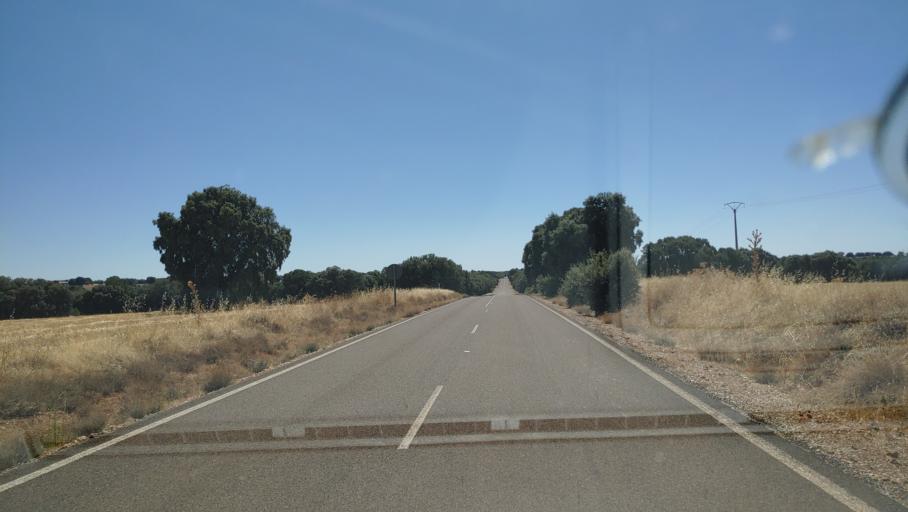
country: ES
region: Castille-La Mancha
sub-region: Provincia de Ciudad Real
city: Villahermosa
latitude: 38.8299
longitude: -2.8264
